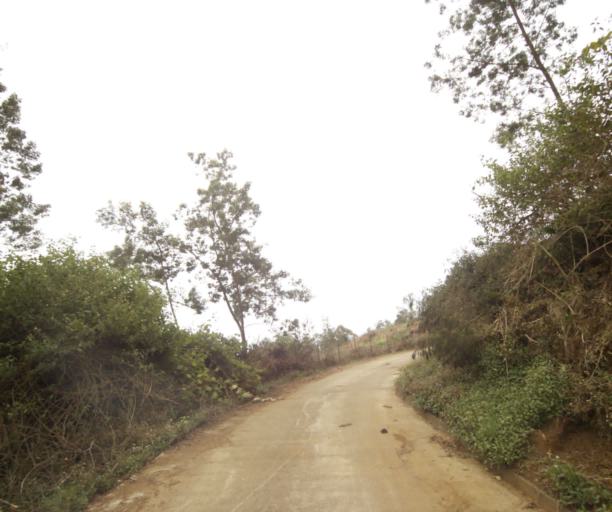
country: RE
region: Reunion
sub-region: Reunion
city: Saint-Paul
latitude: -21.0138
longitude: 55.3572
